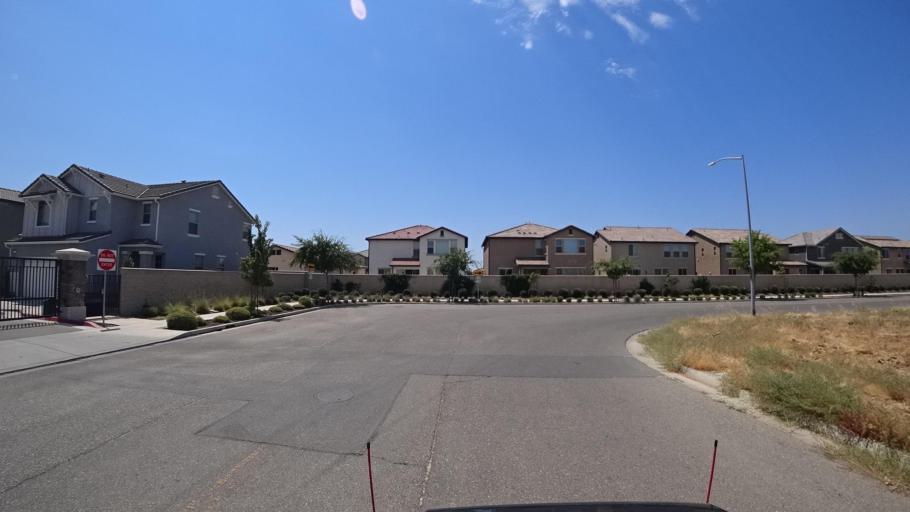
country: US
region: California
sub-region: Fresno County
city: Tarpey Village
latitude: 36.7760
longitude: -119.6795
